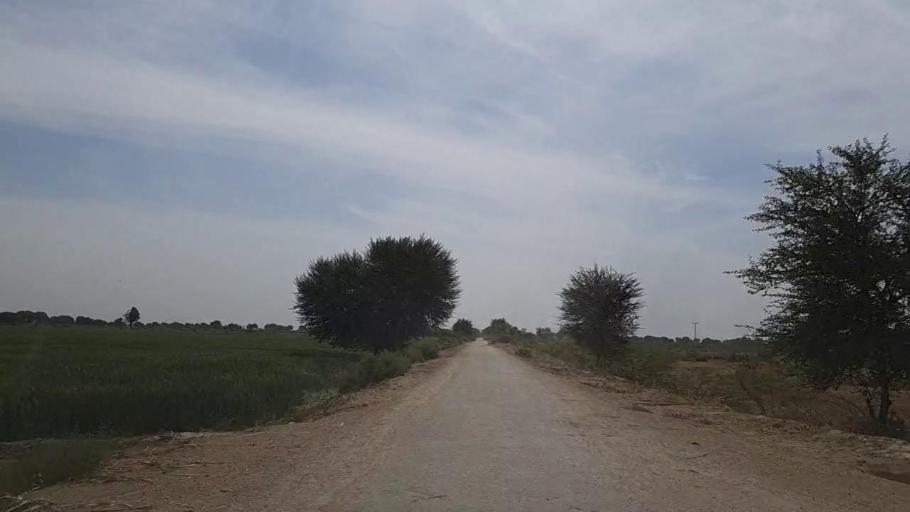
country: PK
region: Sindh
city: Samaro
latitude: 25.2711
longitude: 69.4536
